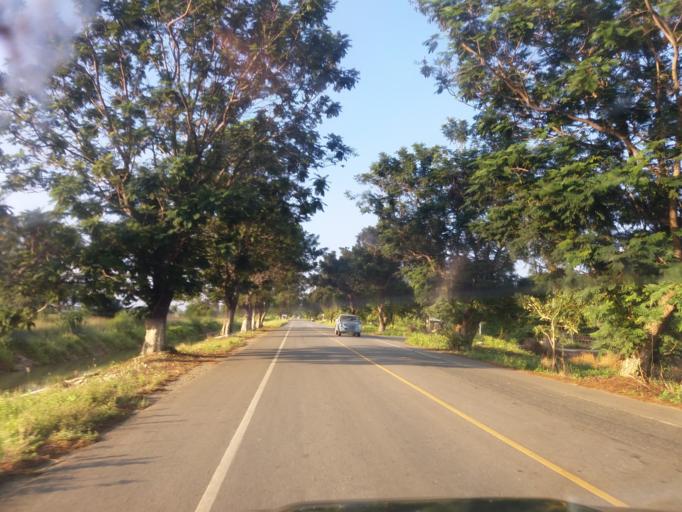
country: TH
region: Suphan Buri
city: Doem Bang Nang Buat
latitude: 14.8721
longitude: 100.0777
